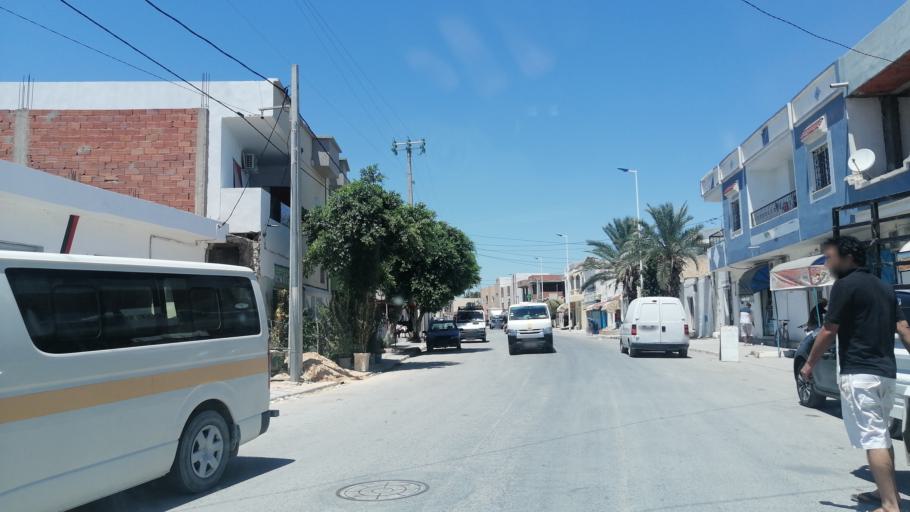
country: TN
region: Al Qayrawan
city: Sbikha
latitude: 36.1205
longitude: 10.0955
